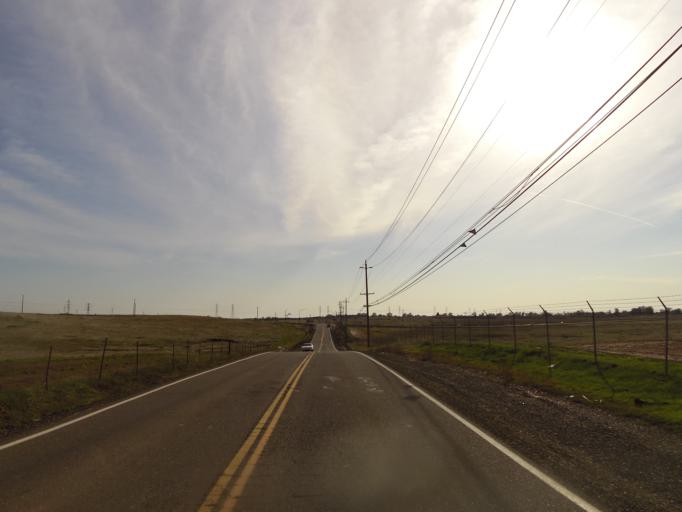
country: US
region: California
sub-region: Sacramento County
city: Folsom
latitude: 38.6184
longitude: -121.1505
